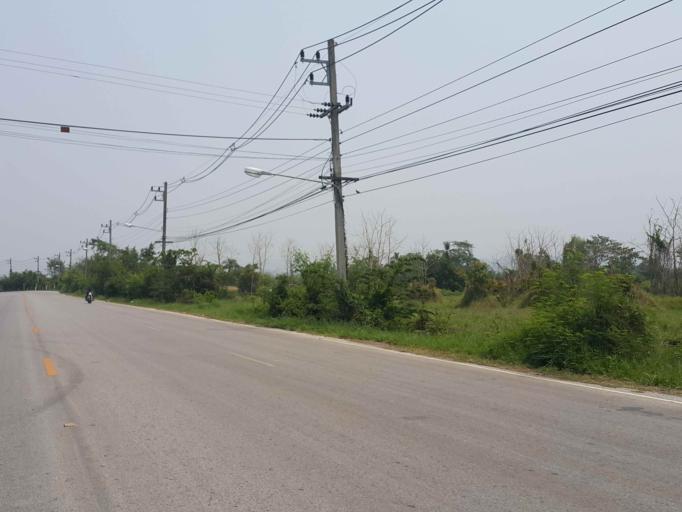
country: TH
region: Chiang Mai
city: San Kamphaeng
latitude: 18.8202
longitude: 99.1246
